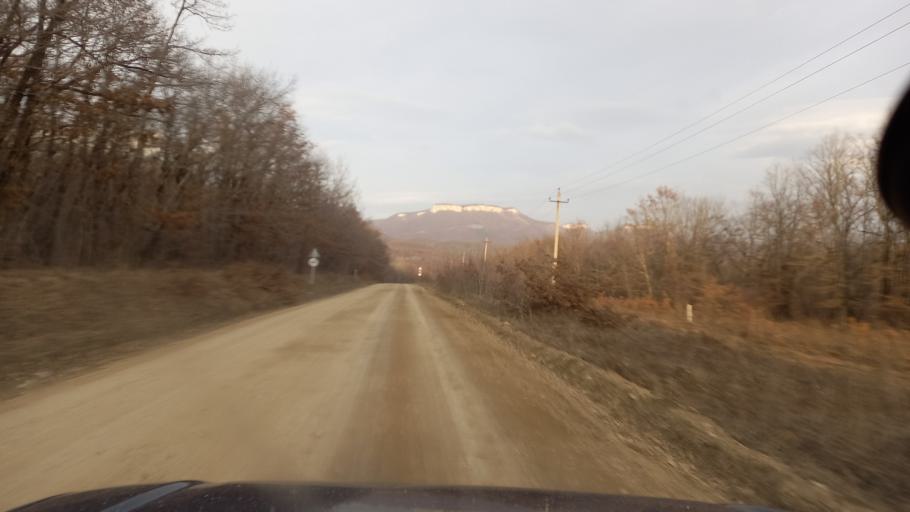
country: RU
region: Adygeya
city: Kamennomostskiy
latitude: 44.2060
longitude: 40.2502
